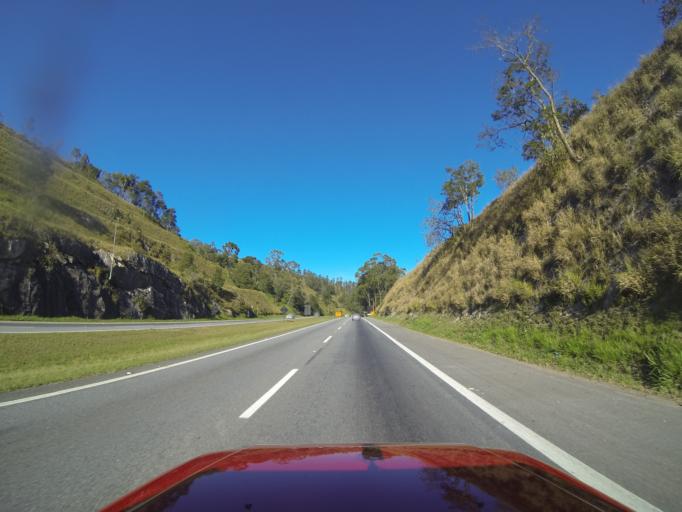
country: BR
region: Sao Paulo
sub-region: Bom Jesus Dos Perdoes
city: Bom Jesus dos Perdoes
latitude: -23.1718
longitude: -46.3890
